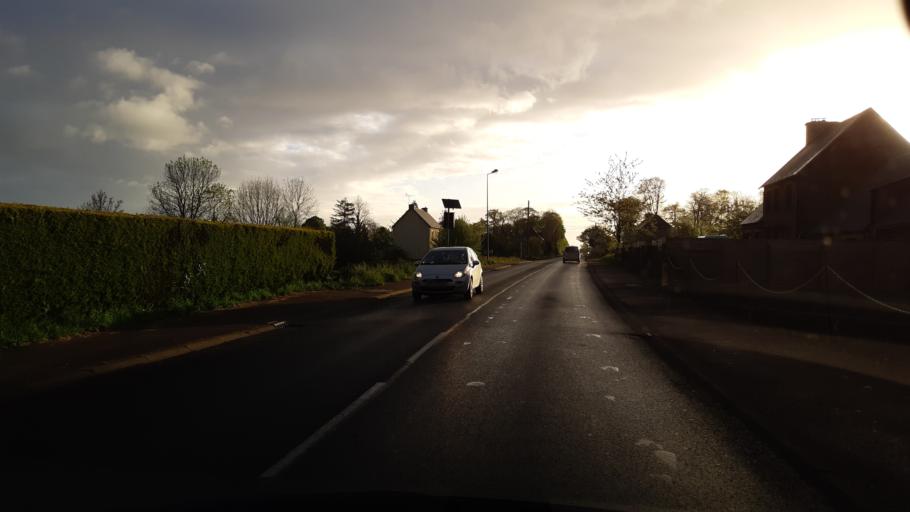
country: FR
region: Lower Normandy
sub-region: Departement de la Manche
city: Agneaux
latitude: 49.0282
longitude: -1.1441
